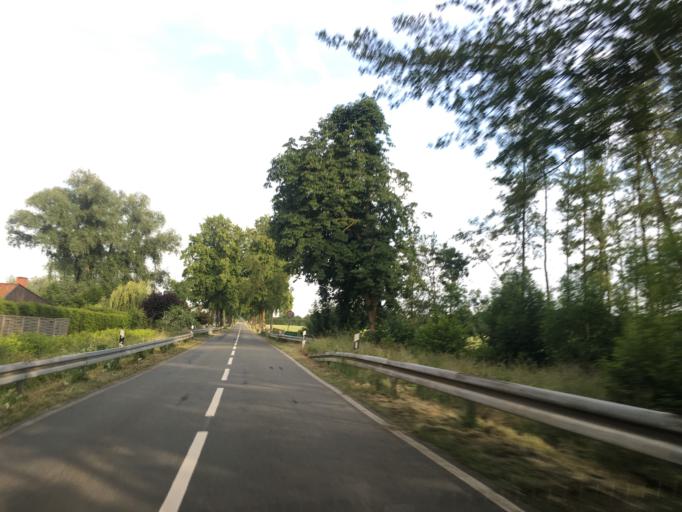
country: DE
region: North Rhine-Westphalia
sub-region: Regierungsbezirk Munster
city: Altenberge
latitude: 51.9803
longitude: 7.5131
